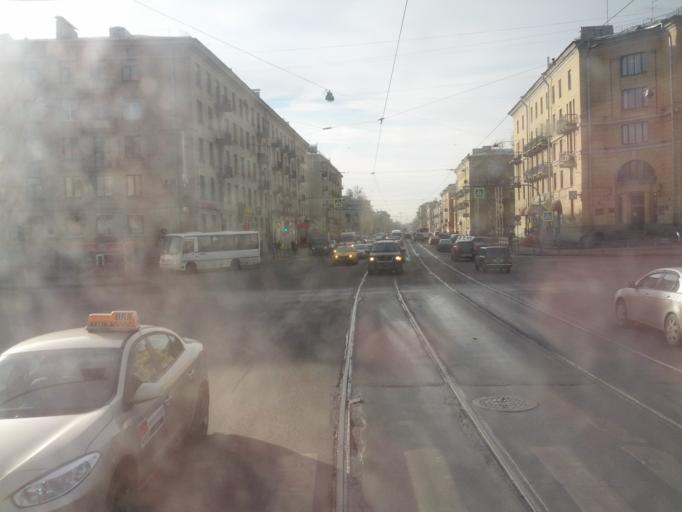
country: RU
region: Leningrad
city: Kalininskiy
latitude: 59.9595
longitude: 30.4157
